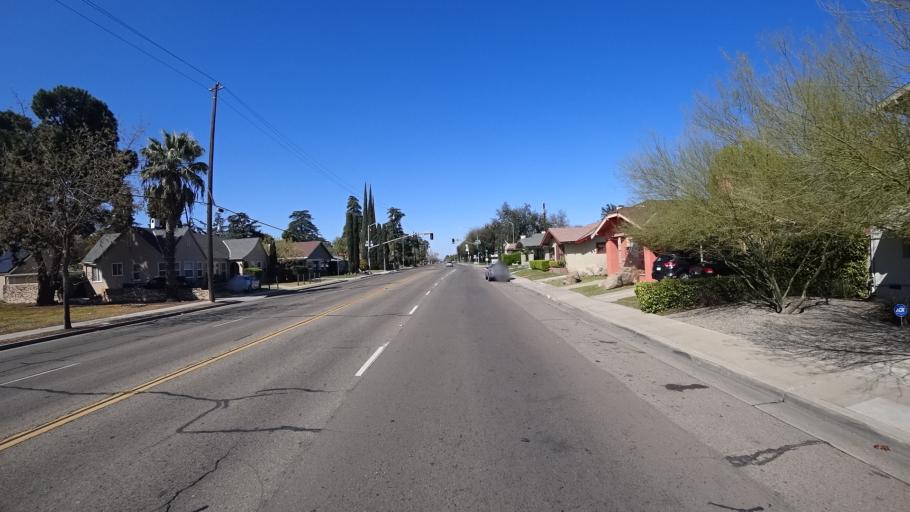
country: US
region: California
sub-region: Fresno County
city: Fresno
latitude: 36.7650
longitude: -119.8031
